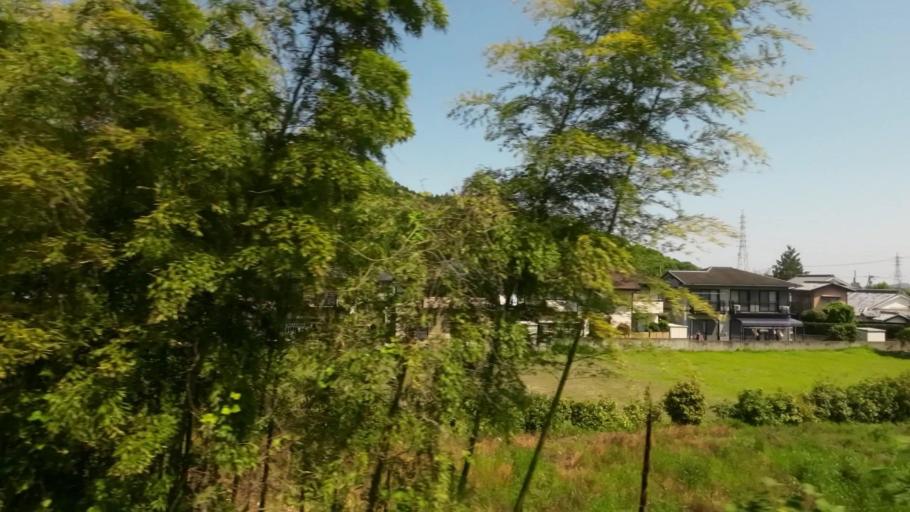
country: JP
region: Ehime
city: Niihama
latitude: 33.9367
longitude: 133.2791
